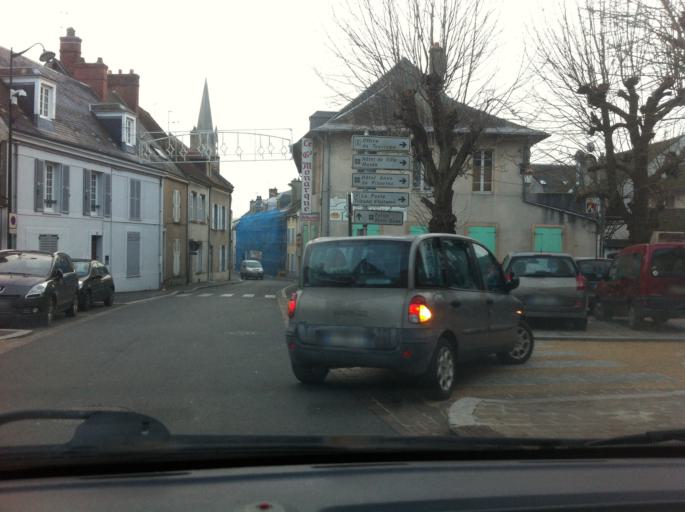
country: FR
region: Ile-de-France
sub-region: Departement de l'Essonne
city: Etampes
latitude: 48.4359
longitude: 2.1615
